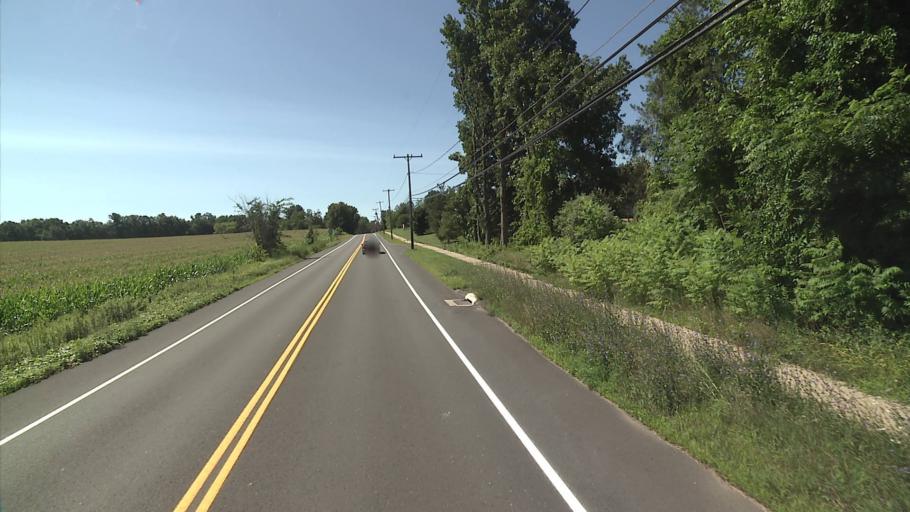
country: US
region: Connecticut
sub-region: Hartford County
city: Salmon Brook
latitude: 41.9583
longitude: -72.7905
